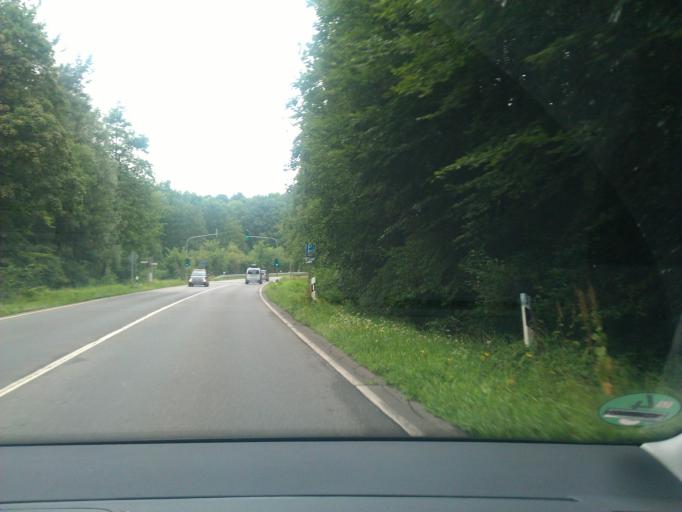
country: DE
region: North Rhine-Westphalia
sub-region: Regierungsbezirk Koln
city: Aachen
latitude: 50.7394
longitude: 6.1088
